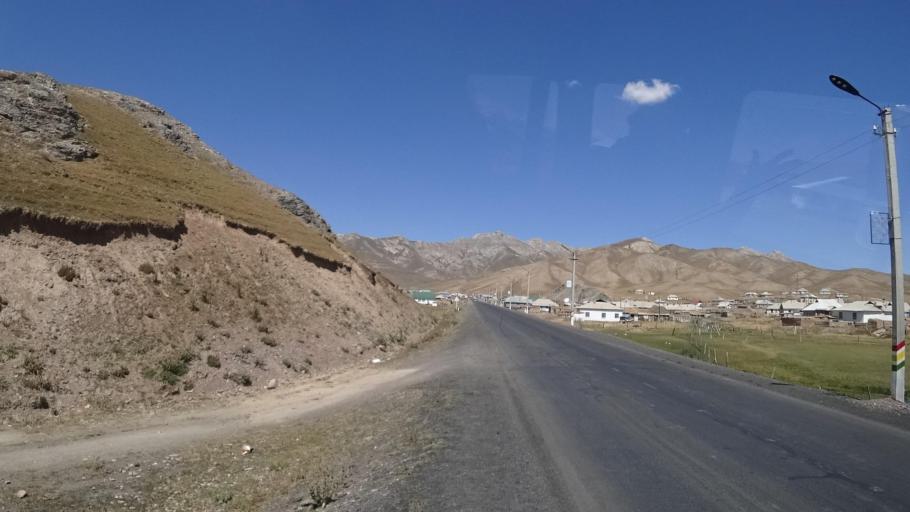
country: KG
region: Osh
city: Gul'cha
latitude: 39.7243
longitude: 73.2484
